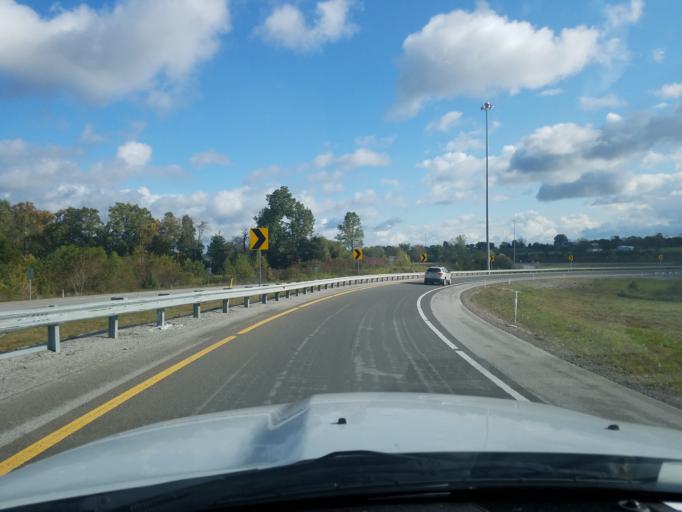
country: US
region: Kentucky
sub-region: Pulaski County
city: Somerset
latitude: 37.1076
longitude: -84.6634
